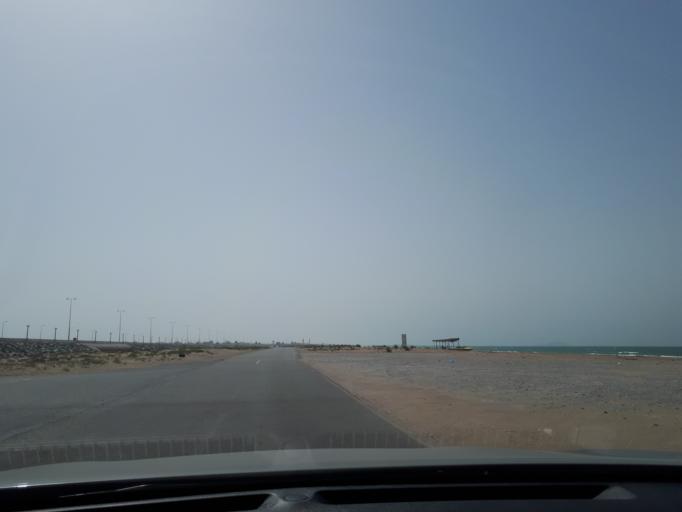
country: OM
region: Al Batinah
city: Barka'
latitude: 23.7146
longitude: 57.8698
